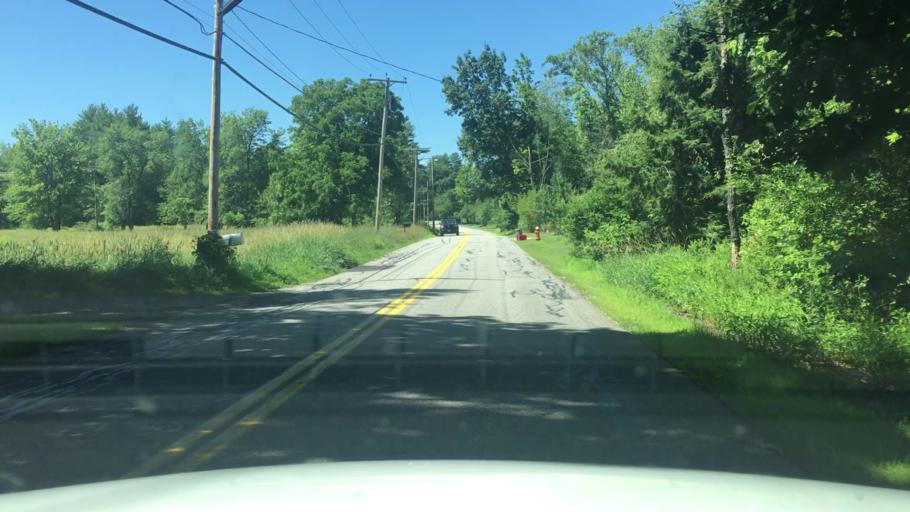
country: US
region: New Hampshire
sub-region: Merrimack County
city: Boscawen
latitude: 43.2682
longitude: -71.6074
